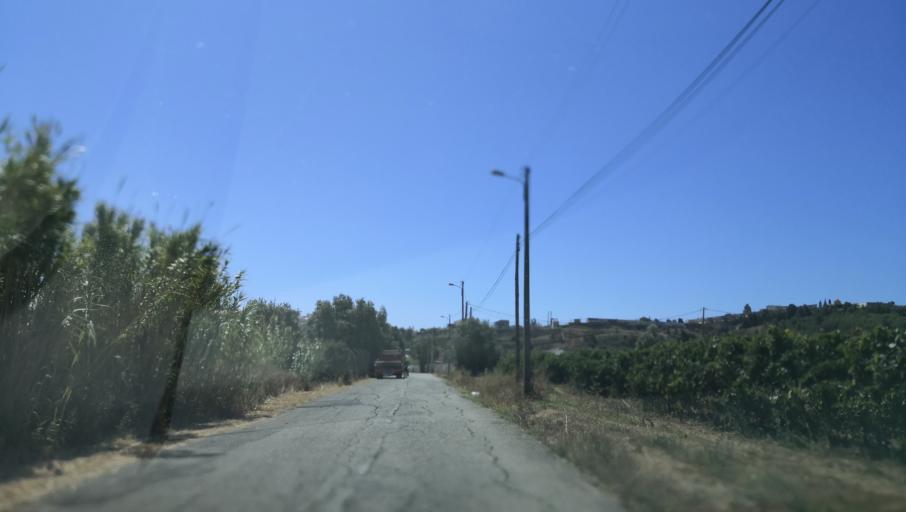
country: PT
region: Setubal
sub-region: Setubal
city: Setubal
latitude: 38.5342
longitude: -8.9138
